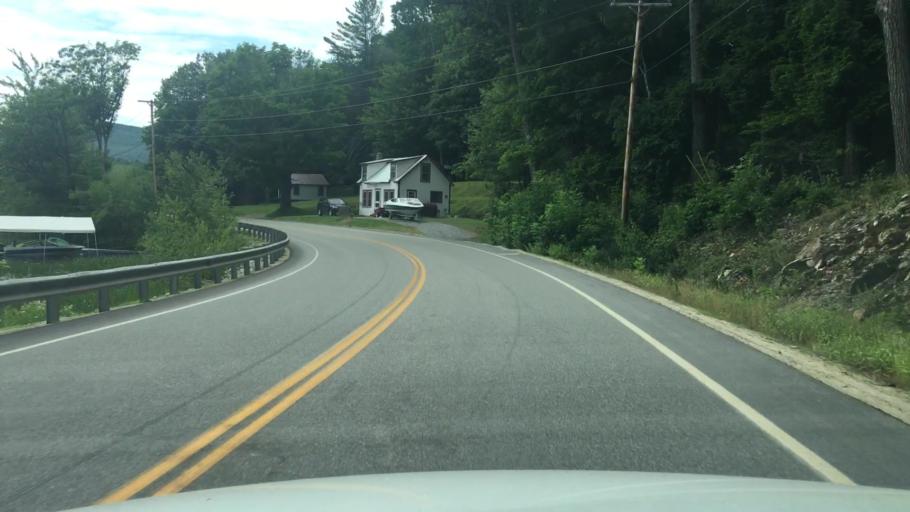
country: US
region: Maine
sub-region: Oxford County
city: Paris
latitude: 44.3705
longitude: -70.4667
